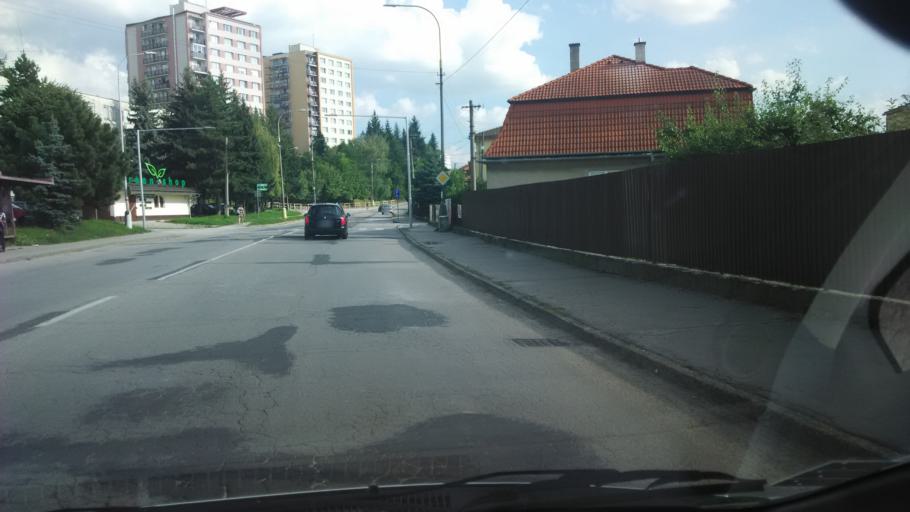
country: SK
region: Nitriansky
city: Banovce nad Bebravou
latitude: 48.7265
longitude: 18.2548
